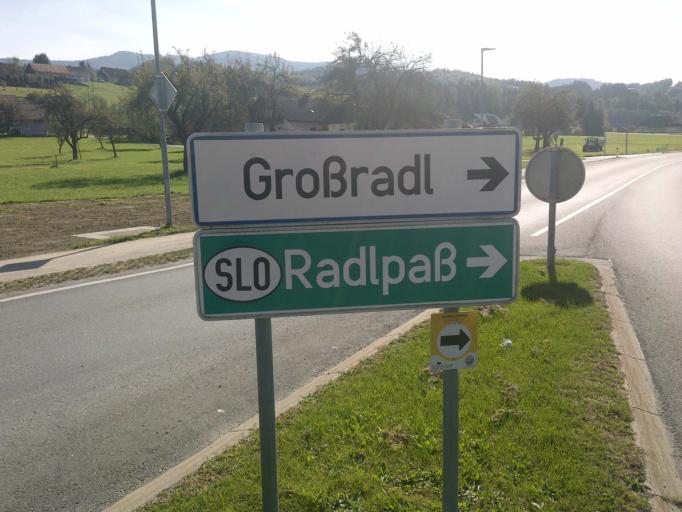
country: AT
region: Styria
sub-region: Politischer Bezirk Deutschlandsberg
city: Aibl
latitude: 46.6808
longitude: 15.2289
